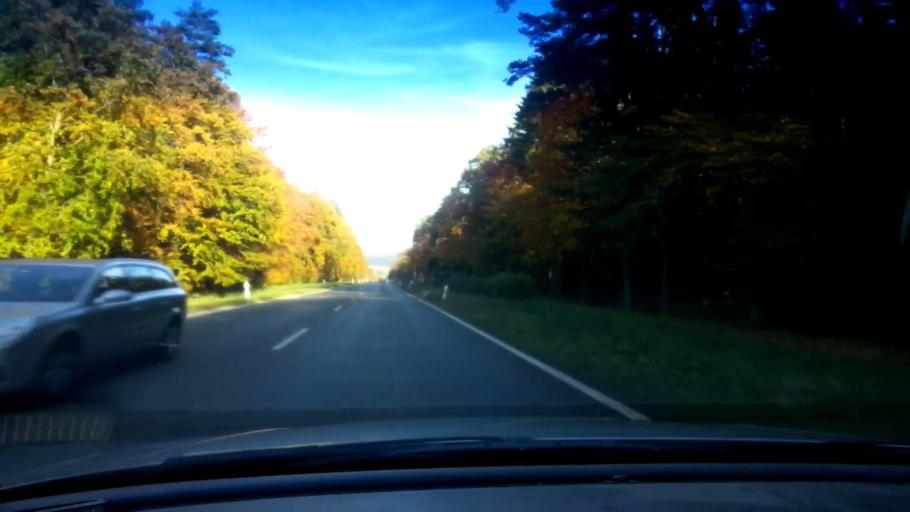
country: DE
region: Bavaria
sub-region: Upper Franconia
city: Memmelsdorf
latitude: 49.9053
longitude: 10.9645
